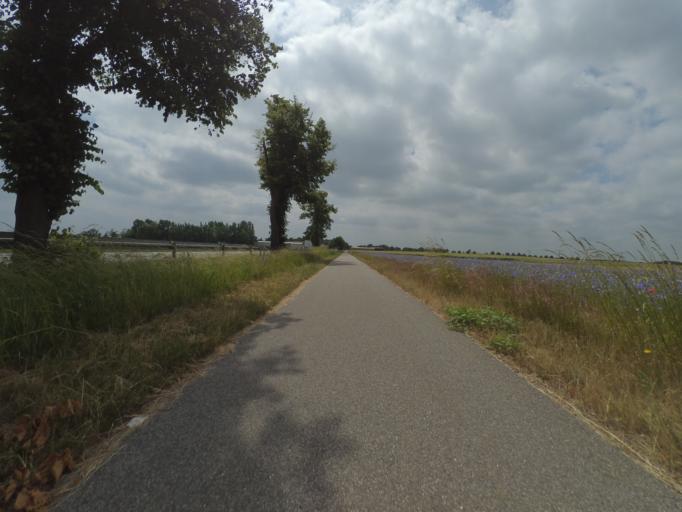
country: DE
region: Mecklenburg-Vorpommern
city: Klink
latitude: 53.4844
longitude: 12.6245
